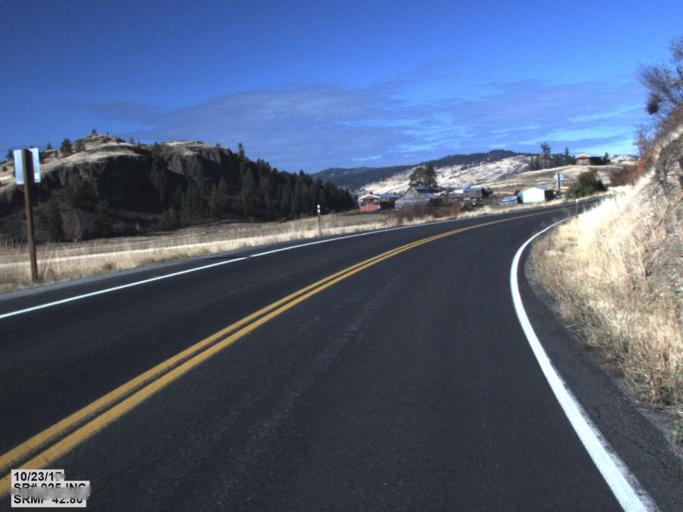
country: US
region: Washington
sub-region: Lincoln County
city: Davenport
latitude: 48.1220
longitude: -118.2089
